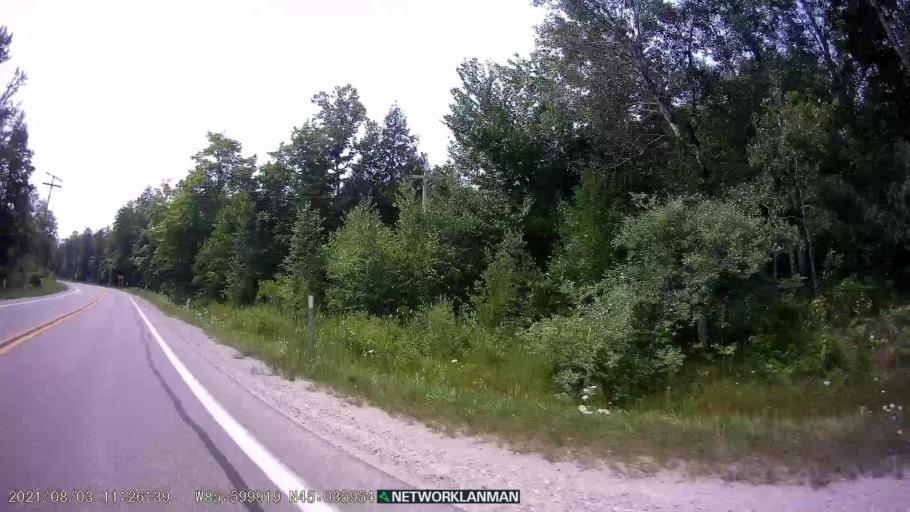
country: US
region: Michigan
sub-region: Leelanau County
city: Leland
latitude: 45.0358
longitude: -85.6004
